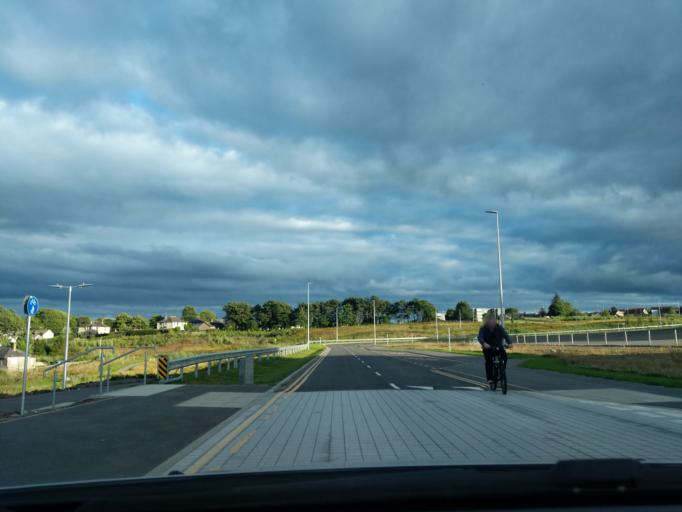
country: GB
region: Scotland
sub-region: Aberdeen City
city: Dyce
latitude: 57.1856
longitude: -2.1872
